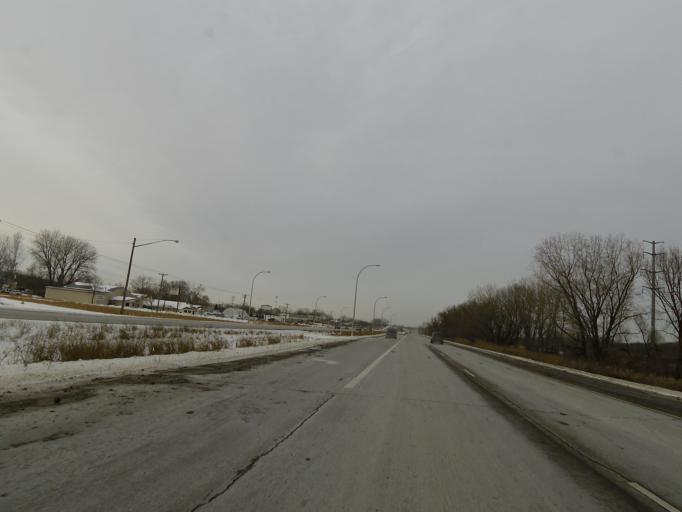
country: US
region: Minnesota
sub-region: Scott County
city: Savage
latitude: 44.7782
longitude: -93.3682
